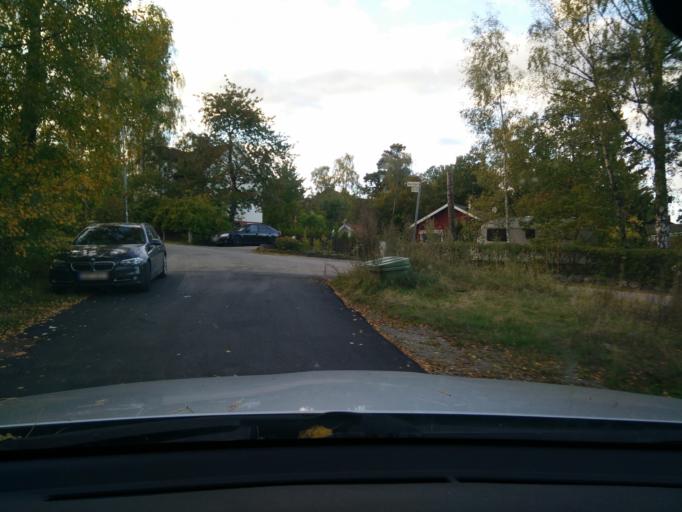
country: SE
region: Stockholm
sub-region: Stockholms Kommun
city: Kista
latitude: 59.4147
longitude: 17.9458
